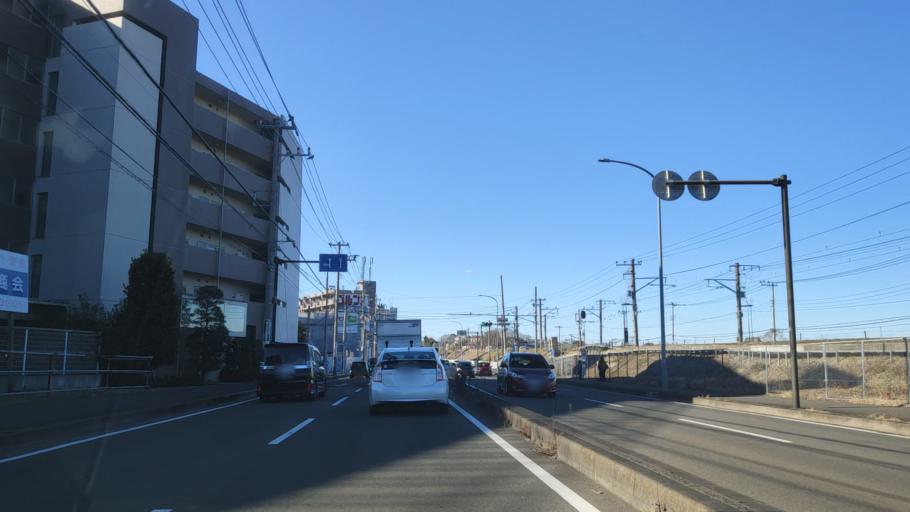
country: JP
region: Tokyo
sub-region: Machida-shi
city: Machida
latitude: 35.5184
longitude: 139.5318
